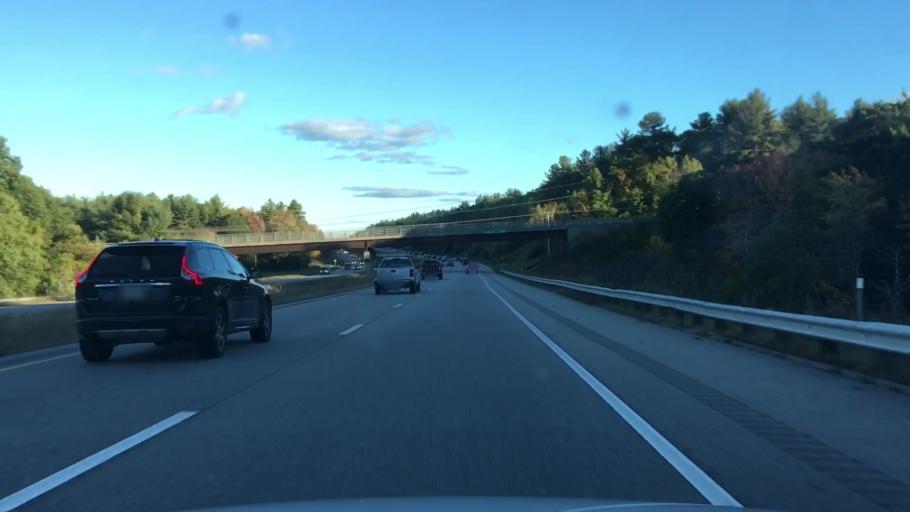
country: US
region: New Hampshire
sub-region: Rockingham County
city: Candia
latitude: 43.0349
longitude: -71.2566
